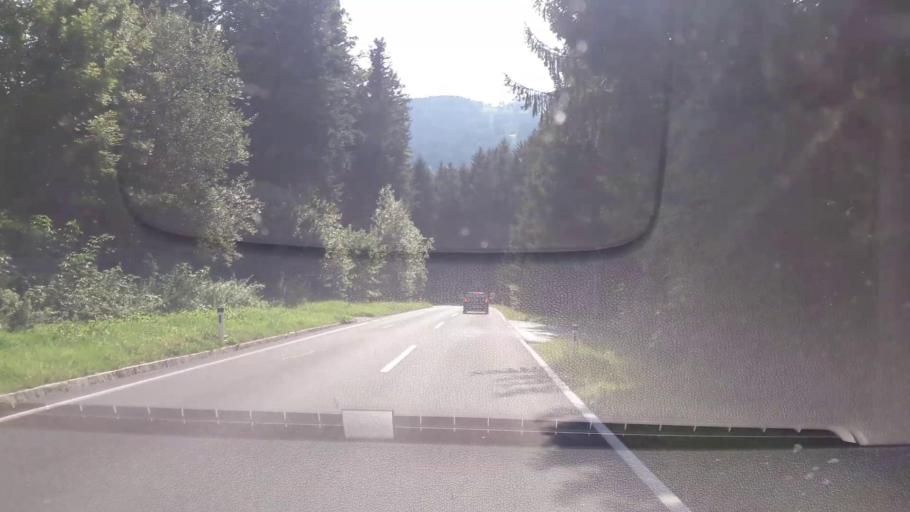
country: AT
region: Styria
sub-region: Politischer Bezirk Weiz
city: Birkfeld
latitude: 47.3467
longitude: 15.6862
